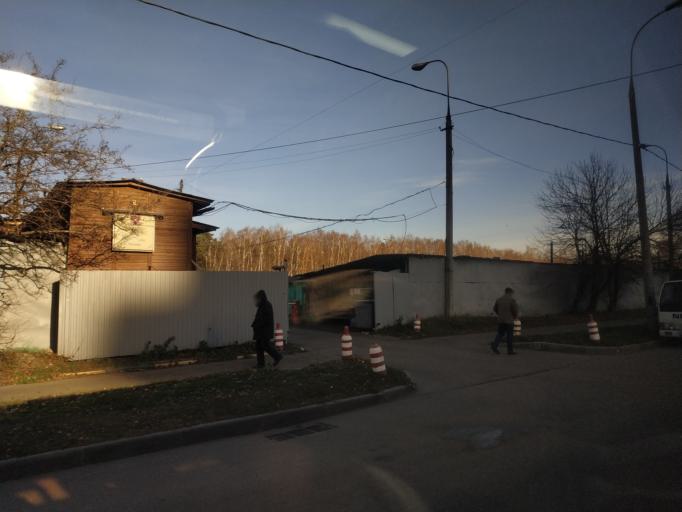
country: RU
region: Moscow
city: Biryulevo
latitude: 55.5859
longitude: 37.6861
